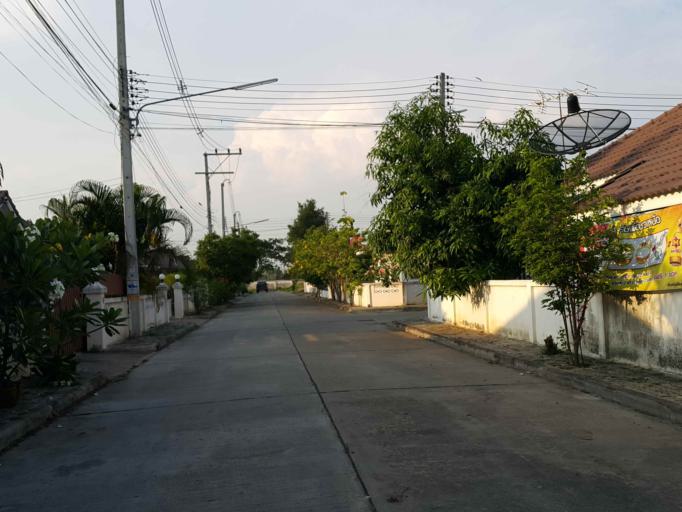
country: TH
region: Chiang Mai
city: Saraphi
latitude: 18.7137
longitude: 98.9763
